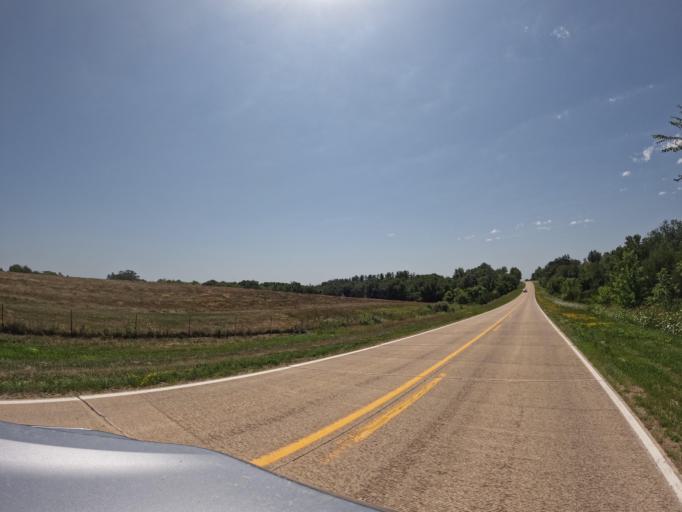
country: US
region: Iowa
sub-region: Henry County
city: Mount Pleasant
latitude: 40.9506
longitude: -91.5545
